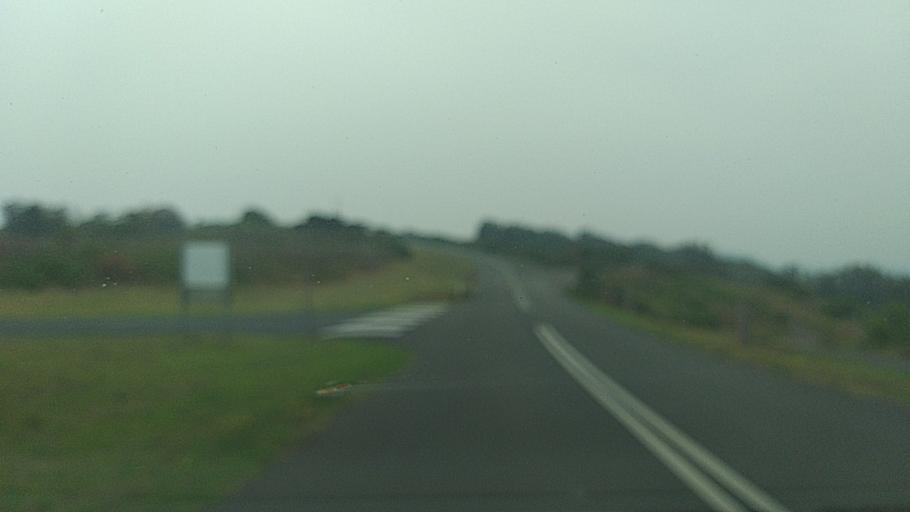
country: AU
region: New South Wales
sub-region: Shellharbour
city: Croom
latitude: -34.6117
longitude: 150.8572
